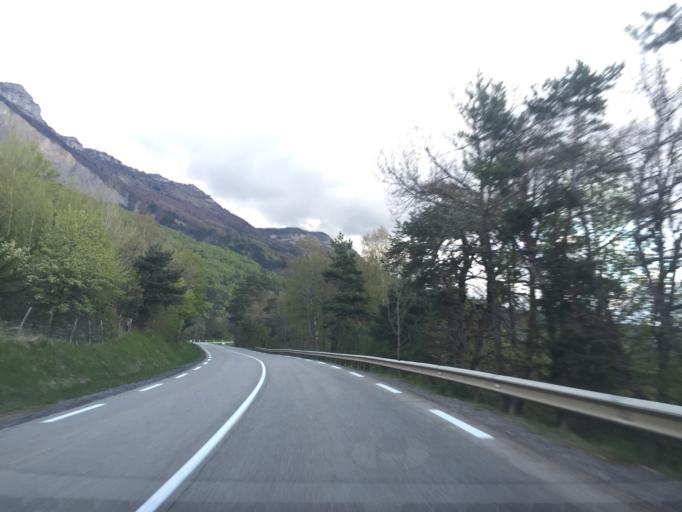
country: FR
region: Rhone-Alpes
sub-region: Departement de l'Isere
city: La Motte-Saint-Martin
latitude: 44.8842
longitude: 5.6182
